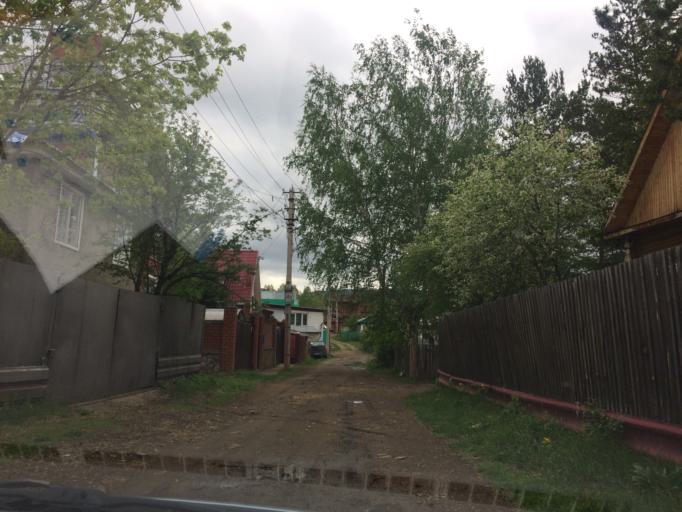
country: RU
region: Bashkortostan
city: Abzakovo
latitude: 53.6074
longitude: 58.6308
